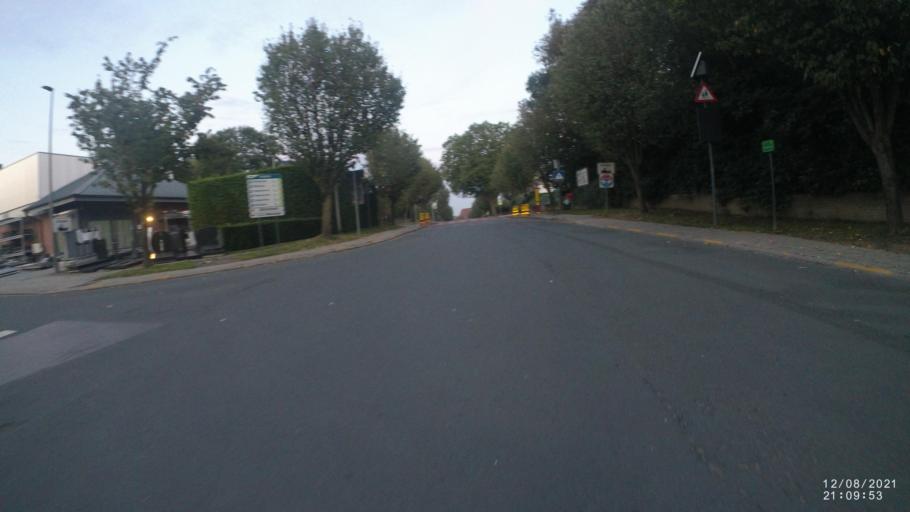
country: BE
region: Flanders
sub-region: Provincie Vlaams-Brabant
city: Dilbeek
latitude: 50.8478
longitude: 4.2562
